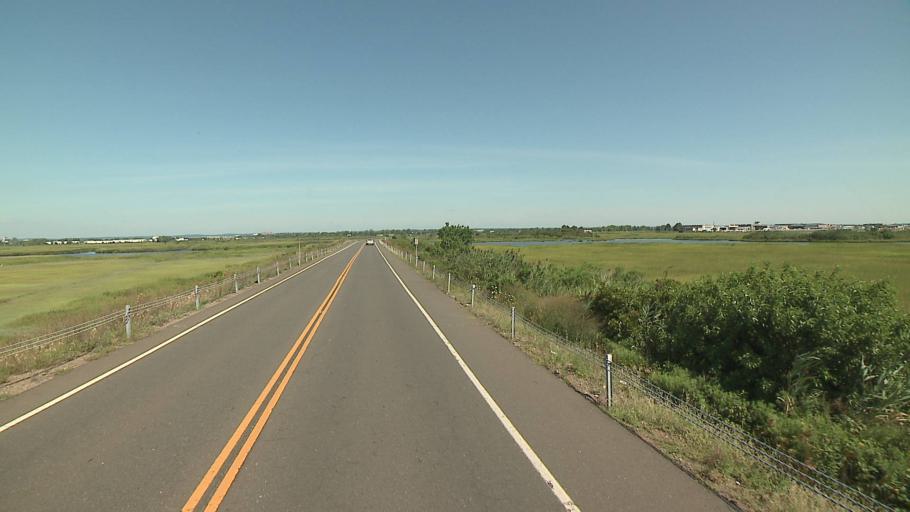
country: US
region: Connecticut
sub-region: Fairfield County
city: Stratford
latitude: 41.1544
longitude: -73.1335
